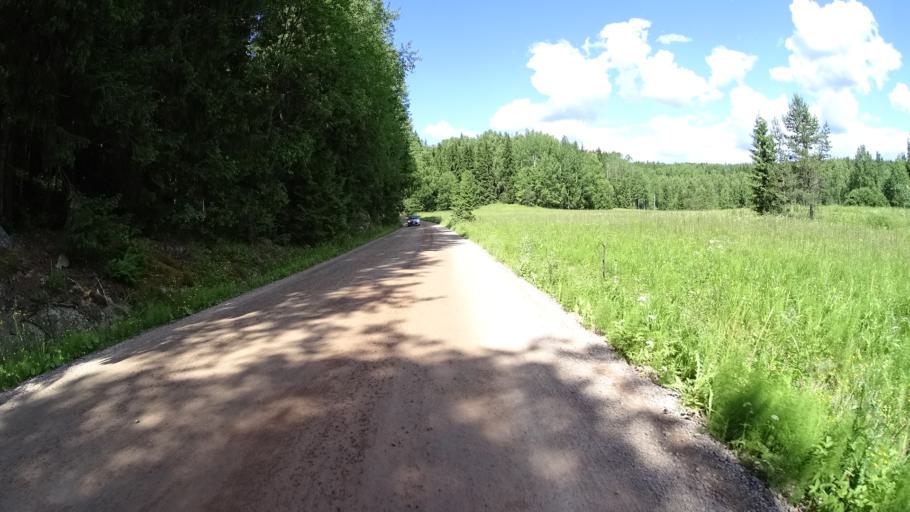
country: FI
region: Uusimaa
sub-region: Helsinki
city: Espoo
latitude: 60.3080
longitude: 24.5295
